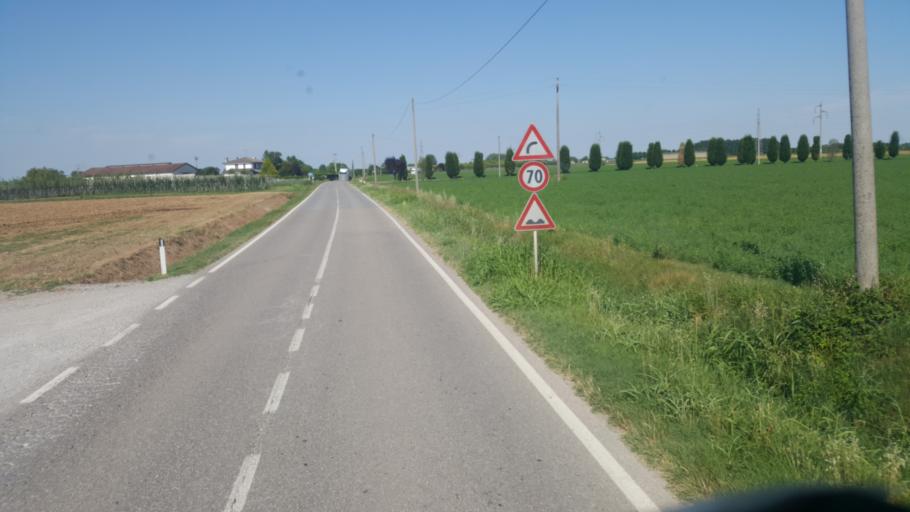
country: IT
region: Lombardy
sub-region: Provincia di Mantova
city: Casalromano
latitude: 45.1951
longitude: 10.3412
